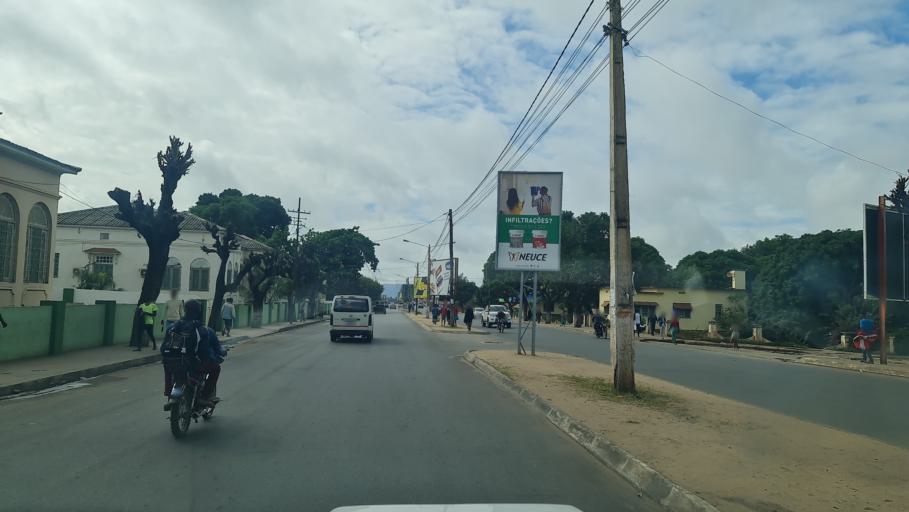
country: MZ
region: Nampula
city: Nampula
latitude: -15.1140
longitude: 39.2683
